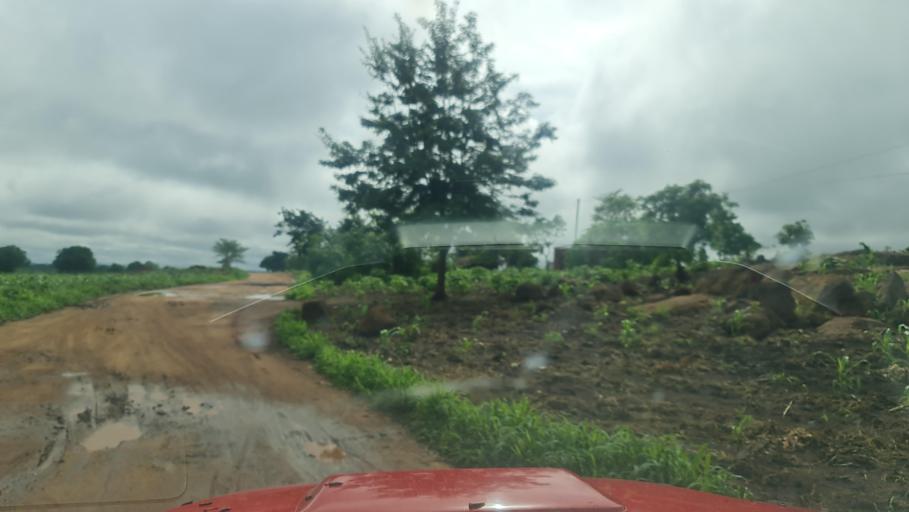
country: MW
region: Southern Region
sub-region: Nsanje District
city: Nsanje
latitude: -17.2227
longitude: 35.6637
